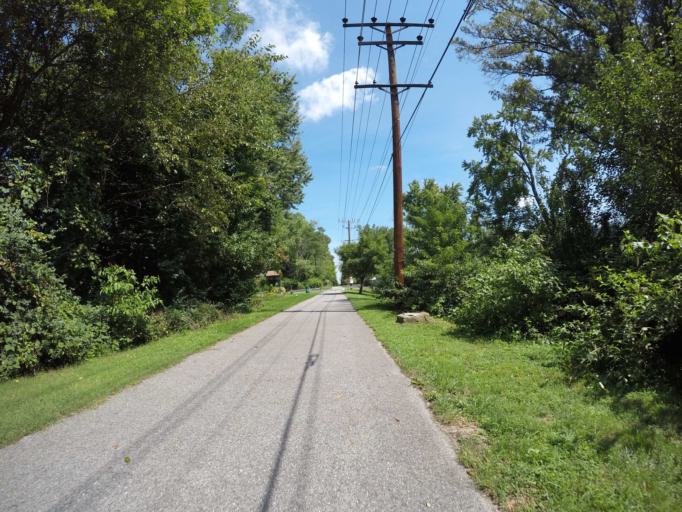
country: US
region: Maryland
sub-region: Anne Arundel County
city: Odenton
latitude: 39.0764
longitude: -76.7028
